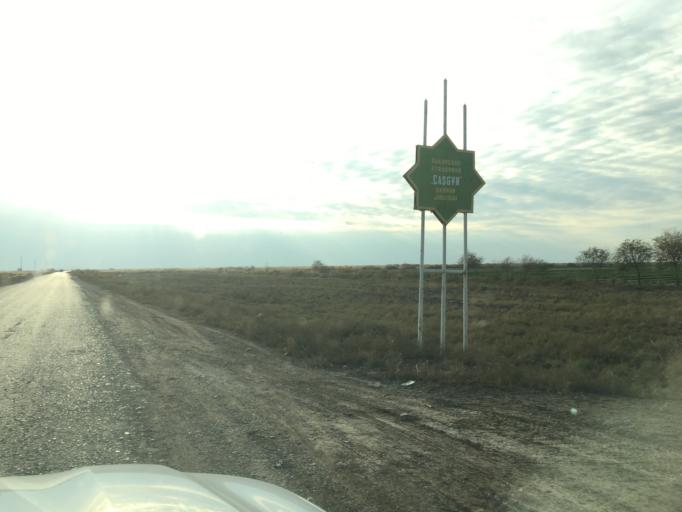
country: TM
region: Ahal
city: Tejen
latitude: 37.4374
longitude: 60.8800
